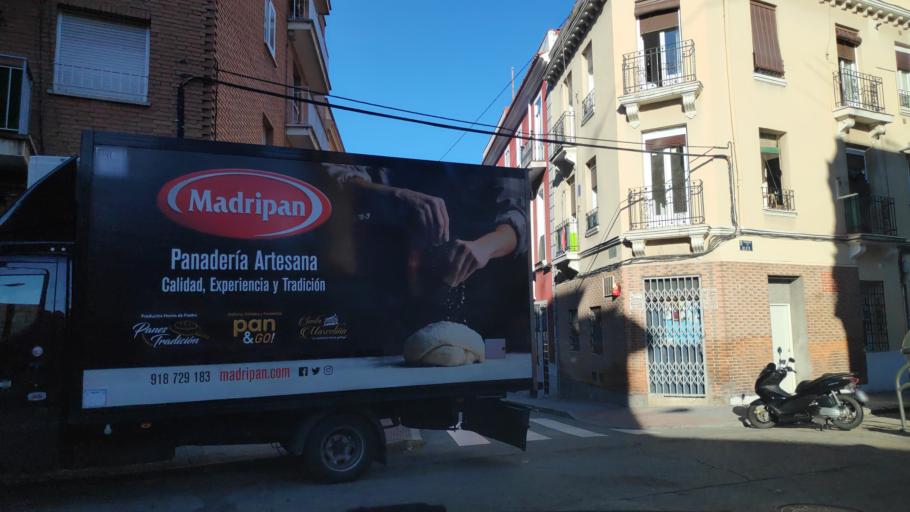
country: ES
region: Madrid
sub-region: Provincia de Madrid
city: Chamberi
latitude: 40.4505
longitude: -3.7073
